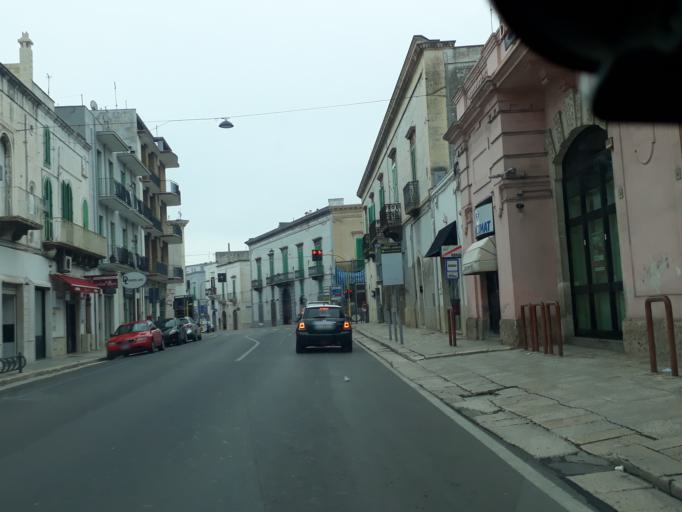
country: IT
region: Apulia
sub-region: Provincia di Brindisi
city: Fasano
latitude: 40.8360
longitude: 17.3615
